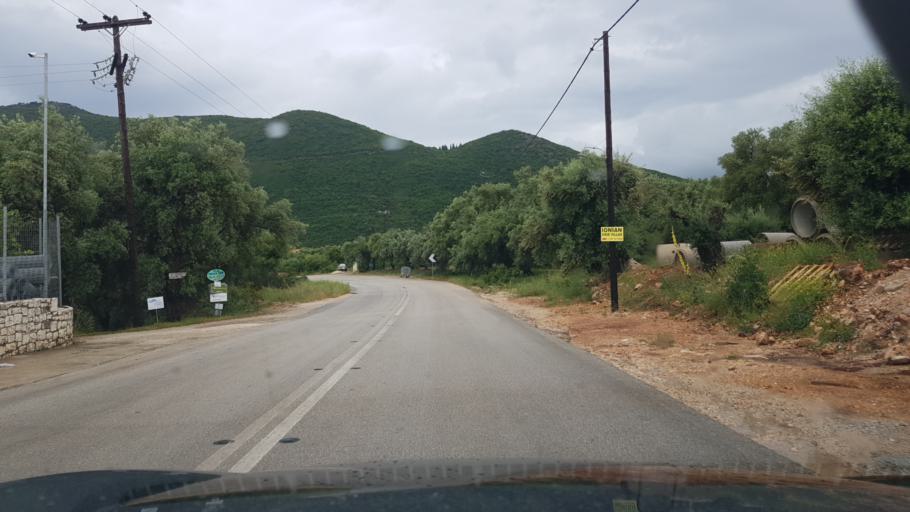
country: GR
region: Ionian Islands
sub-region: Lefkada
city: Nidri
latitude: 38.6355
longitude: 20.6715
